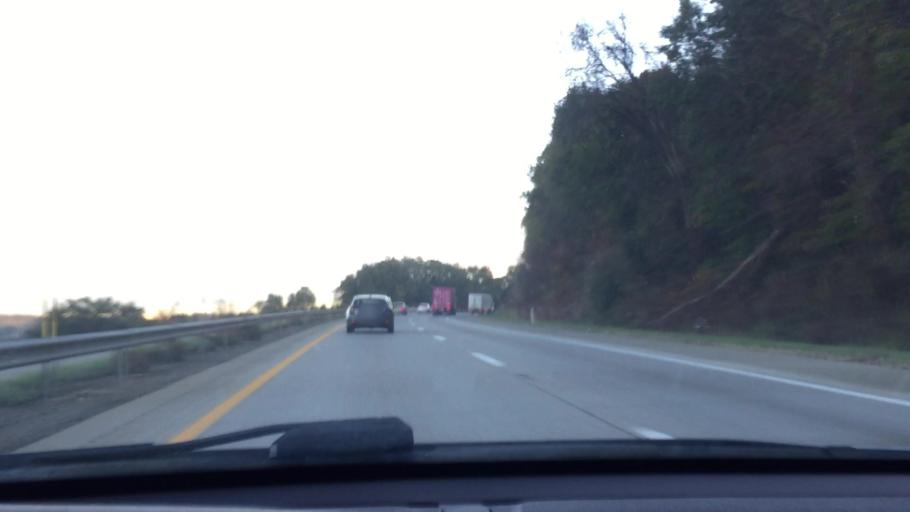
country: US
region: Pennsylvania
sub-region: Washington County
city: Canonsburg
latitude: 40.2619
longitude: -80.1718
